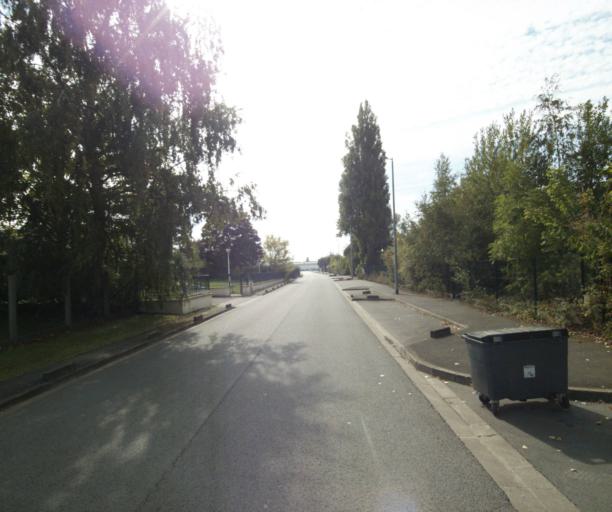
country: FR
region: Nord-Pas-de-Calais
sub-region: Departement du Nord
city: Seclin
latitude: 50.5605
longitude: 3.0399
